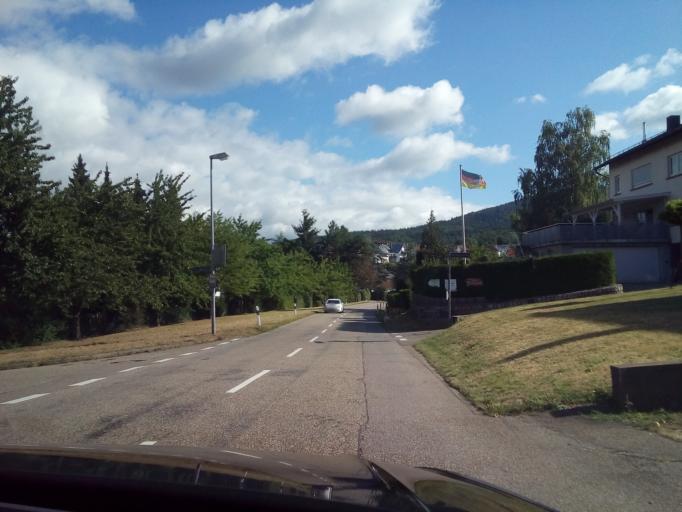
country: DE
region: Baden-Wuerttemberg
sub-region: Karlsruhe Region
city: Sinzheim
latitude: 48.7360
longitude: 8.1756
